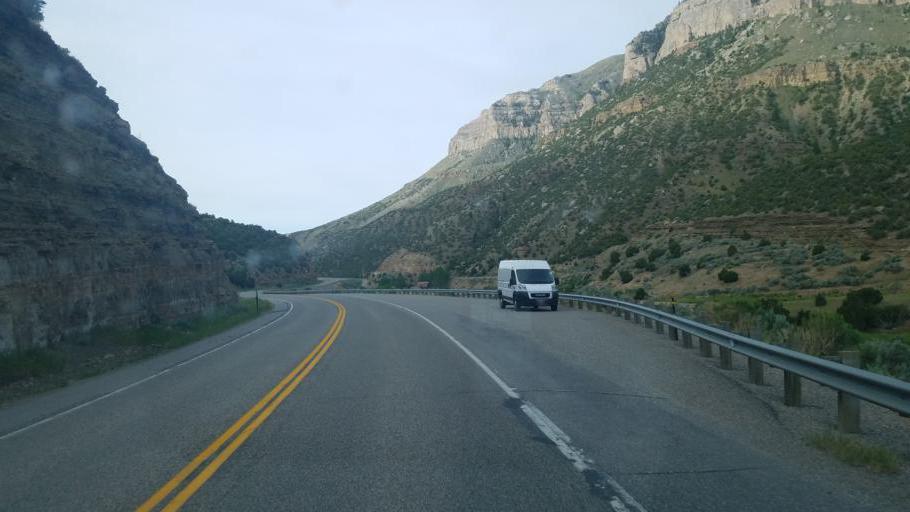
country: US
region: Wyoming
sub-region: Hot Springs County
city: Thermopolis
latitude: 43.4727
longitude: -108.1709
